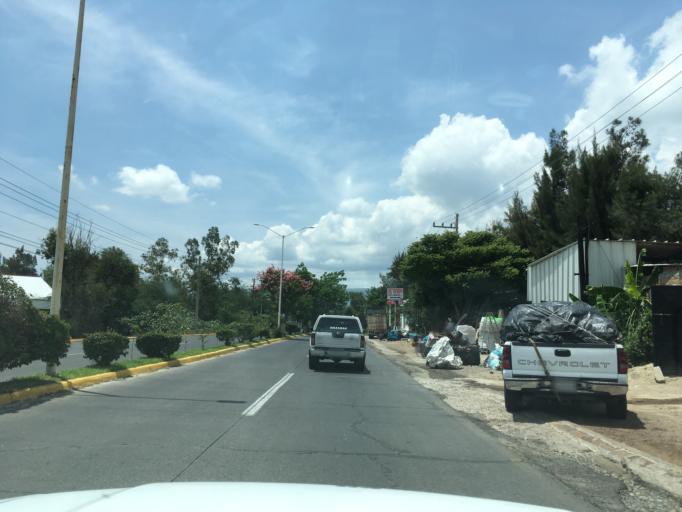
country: MX
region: Jalisco
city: Tlajomulco de Zuniga
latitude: 20.4668
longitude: -103.4499
